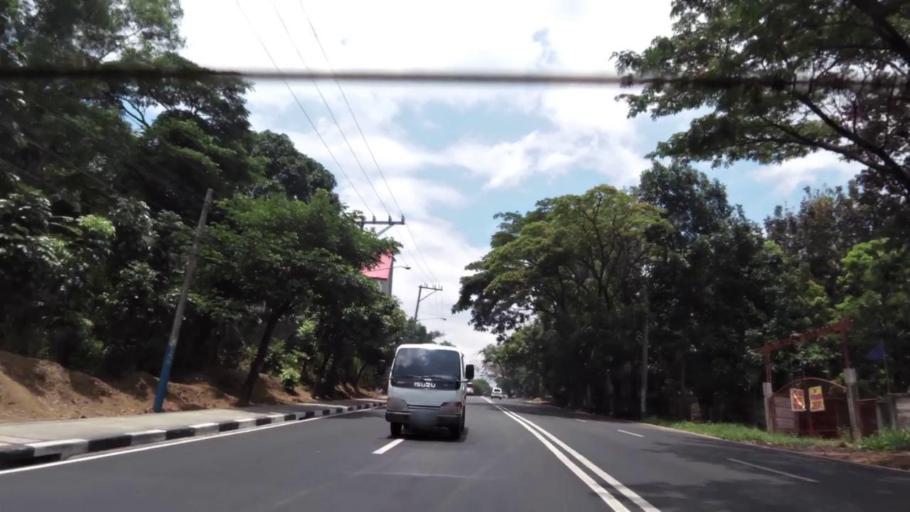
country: PH
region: Calabarzon
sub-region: Province of Rizal
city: Antipolo
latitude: 14.6105
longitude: 121.1593
